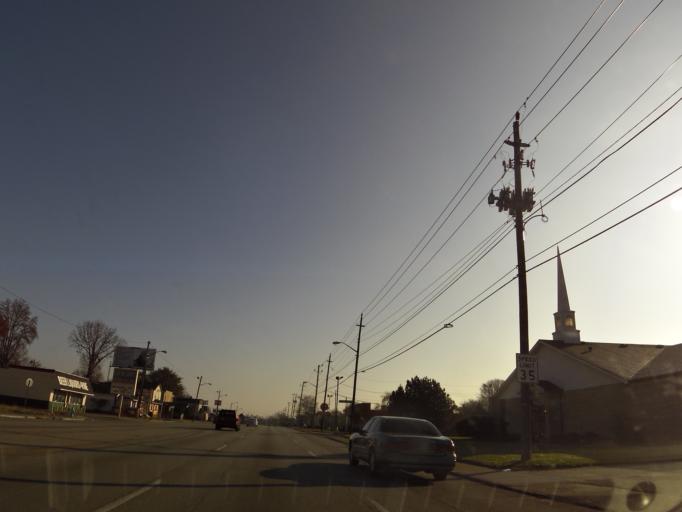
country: US
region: Indiana
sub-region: Marion County
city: Indianapolis
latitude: 39.7879
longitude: -86.2103
